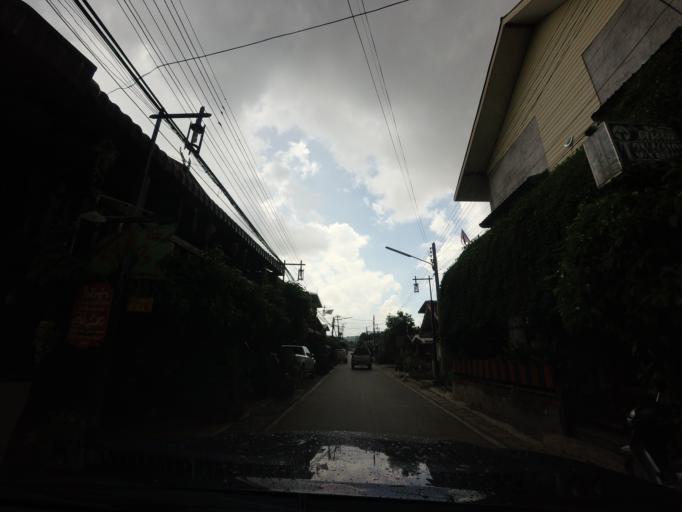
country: TH
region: Loei
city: Chiang Khan
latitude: 17.8929
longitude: 101.6497
